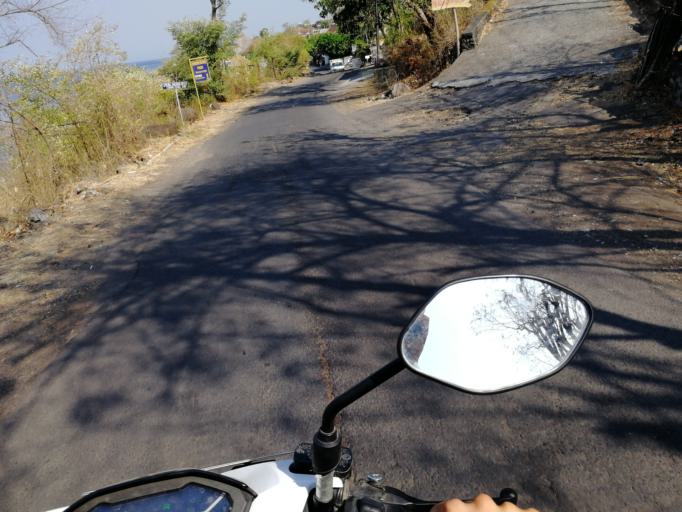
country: ID
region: Bali
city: Biaslantang Kaler
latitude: -8.3452
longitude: 115.6754
